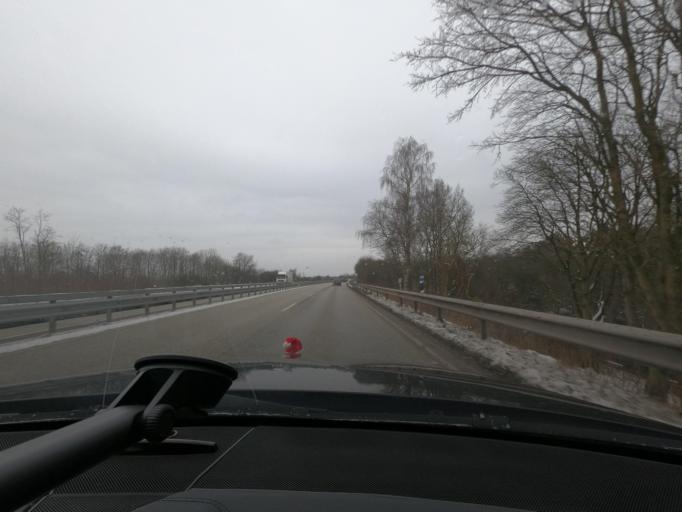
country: DE
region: Schleswig-Holstein
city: Flensburg
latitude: 54.7776
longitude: 9.4094
